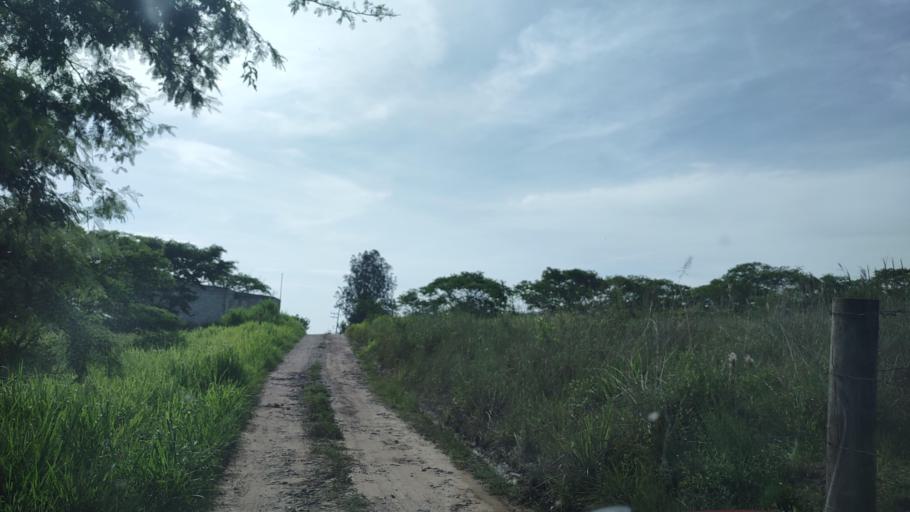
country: MX
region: Veracruz
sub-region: Emiliano Zapata
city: Dos Rios
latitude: 19.4723
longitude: -96.8248
